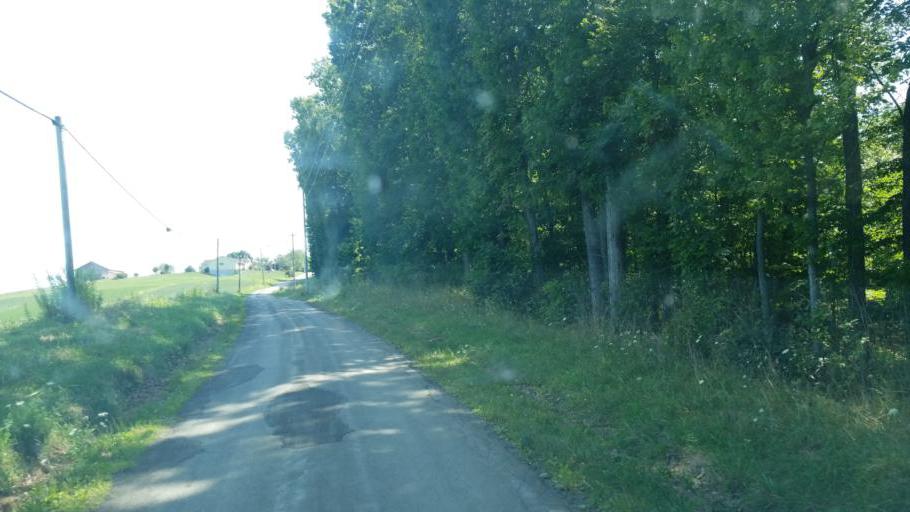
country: US
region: Pennsylvania
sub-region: Clarion County
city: Knox
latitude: 41.0986
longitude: -79.5234
